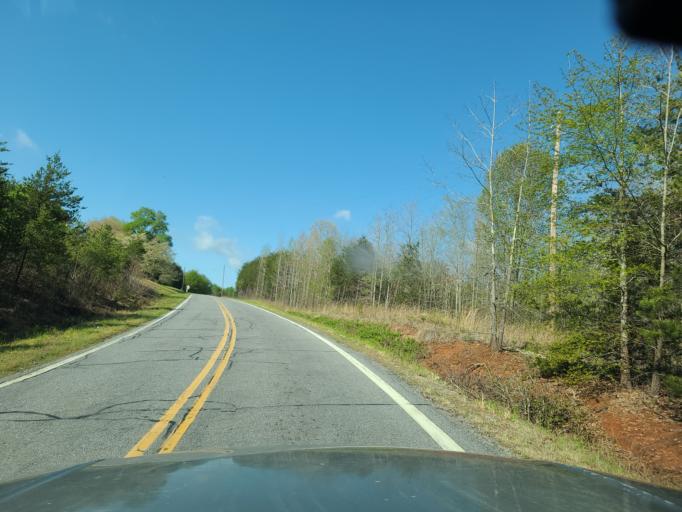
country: US
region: North Carolina
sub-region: Rutherford County
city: Spindale
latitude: 35.4034
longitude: -81.8806
